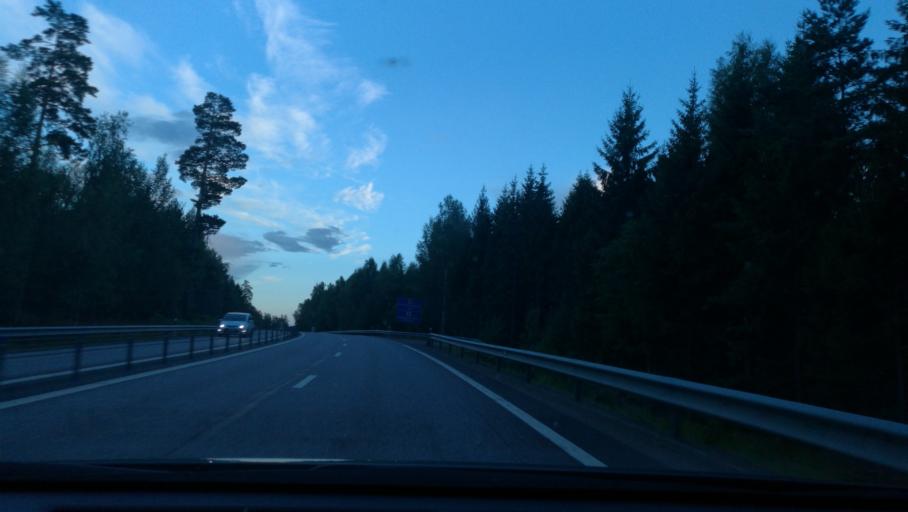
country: SE
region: Soedermanland
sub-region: Katrineholms Kommun
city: Katrineholm
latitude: 58.8398
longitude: 16.1957
